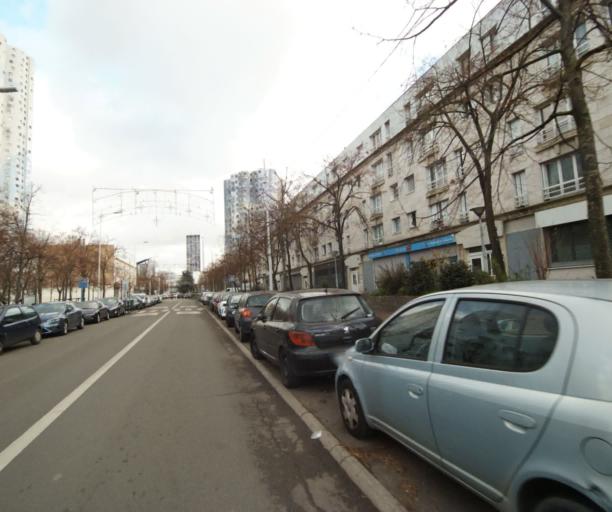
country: FR
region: Ile-de-France
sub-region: Departement des Hauts-de-Seine
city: La Defense
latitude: 48.8884
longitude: 2.2255
